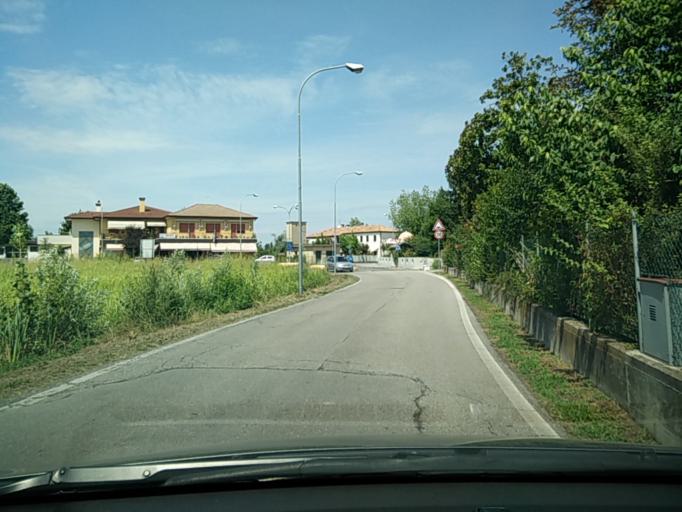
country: IT
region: Veneto
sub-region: Provincia di Venezia
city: San Dona di Piave
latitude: 45.6085
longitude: 12.5770
